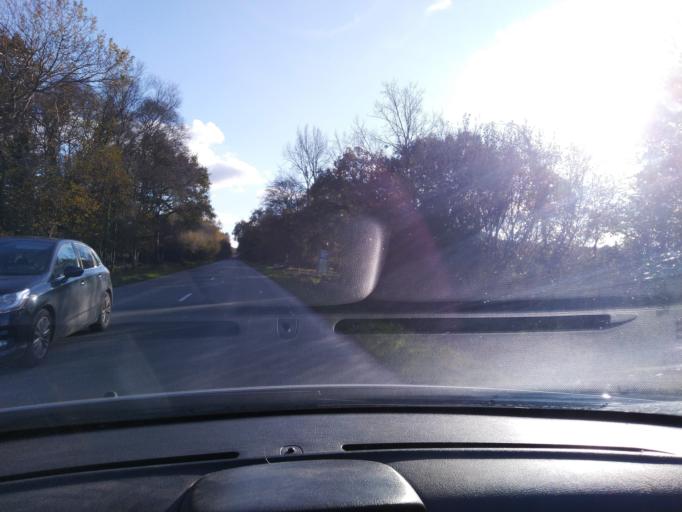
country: FR
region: Brittany
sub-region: Departement des Cotes-d'Armor
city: Plestin-les-Greves
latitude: 48.6187
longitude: -3.6199
